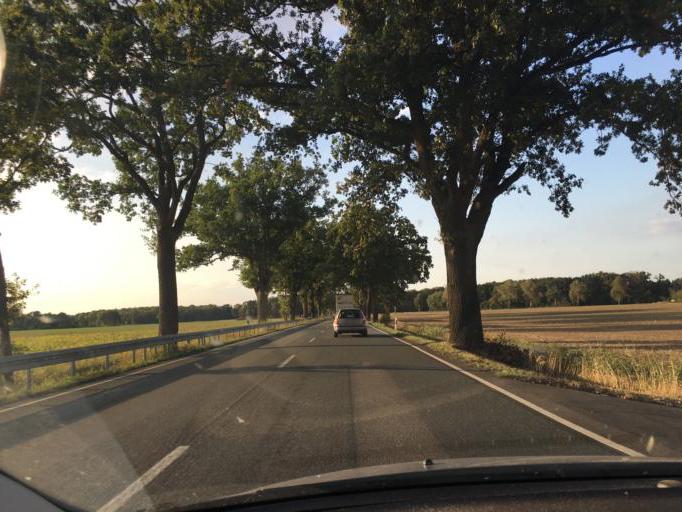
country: DE
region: Lower Saxony
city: Nienhagen
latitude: 52.5673
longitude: 10.1329
